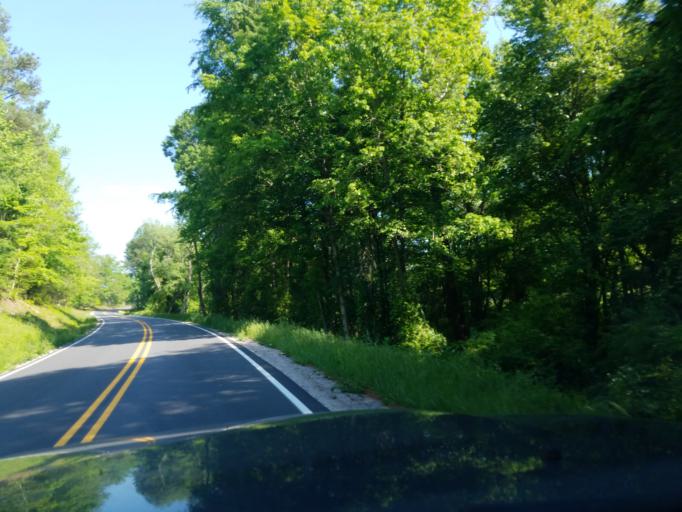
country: US
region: North Carolina
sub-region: Vance County
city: Henderson
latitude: 36.3855
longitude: -78.4465
